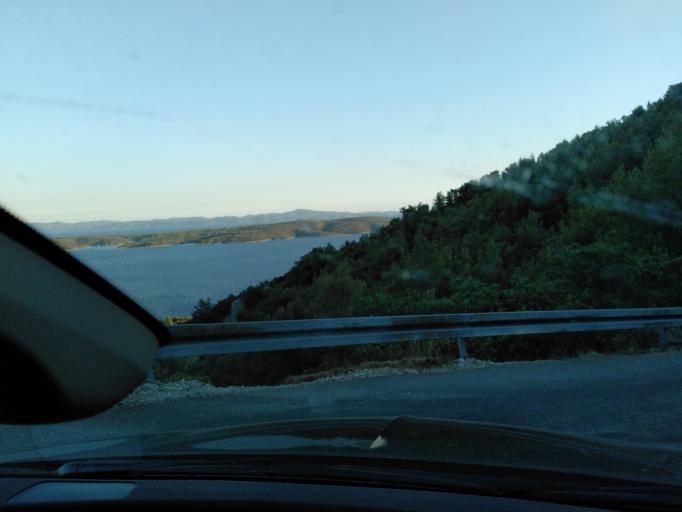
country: HR
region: Splitsko-Dalmatinska
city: Jelsa
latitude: 43.1281
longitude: 16.6814
